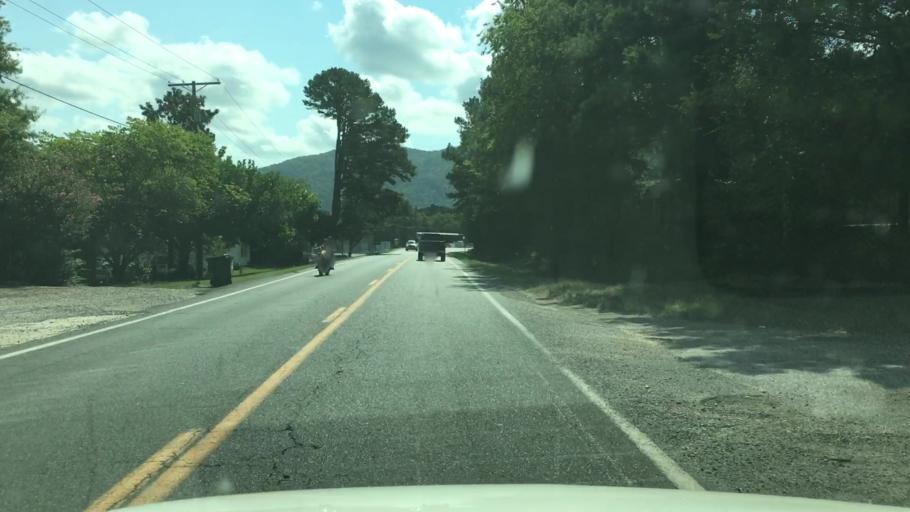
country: US
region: Arkansas
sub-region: Garland County
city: Piney
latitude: 34.5076
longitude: -93.1336
